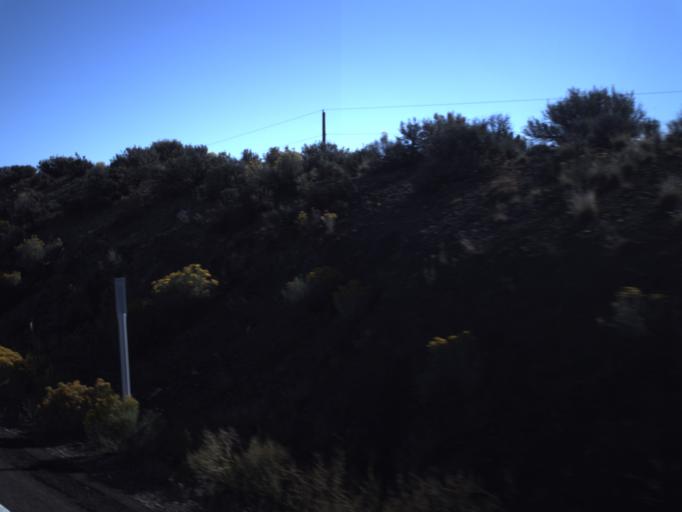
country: US
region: Utah
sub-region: Washington County
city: Enterprise
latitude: 37.7367
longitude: -114.0196
